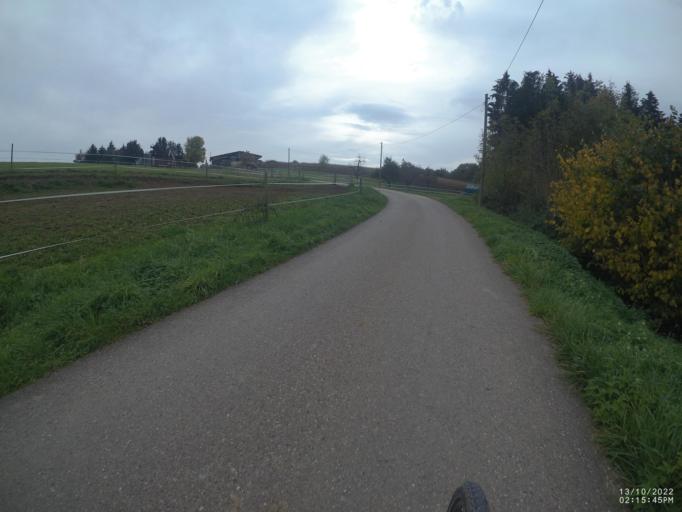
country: DE
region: Baden-Wuerttemberg
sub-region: Regierungsbezirk Stuttgart
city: Albershausen
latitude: 48.6857
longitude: 9.5593
